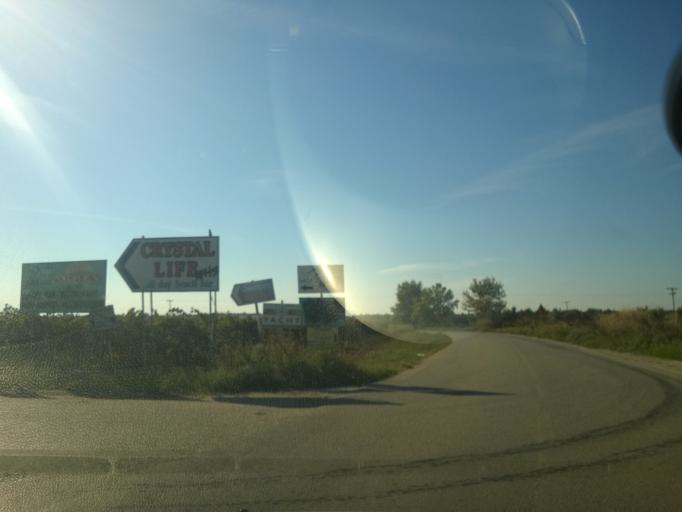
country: GR
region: Central Macedonia
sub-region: Nomos Chalkidikis
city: Nea Kallikrateia
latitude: 40.3399
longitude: 23.0467
